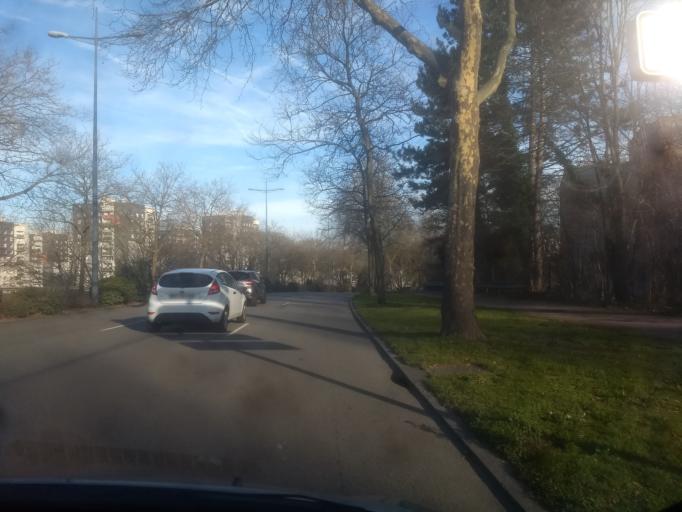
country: FR
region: Limousin
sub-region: Departement de la Haute-Vienne
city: Isle
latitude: 45.8314
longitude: 1.2253
